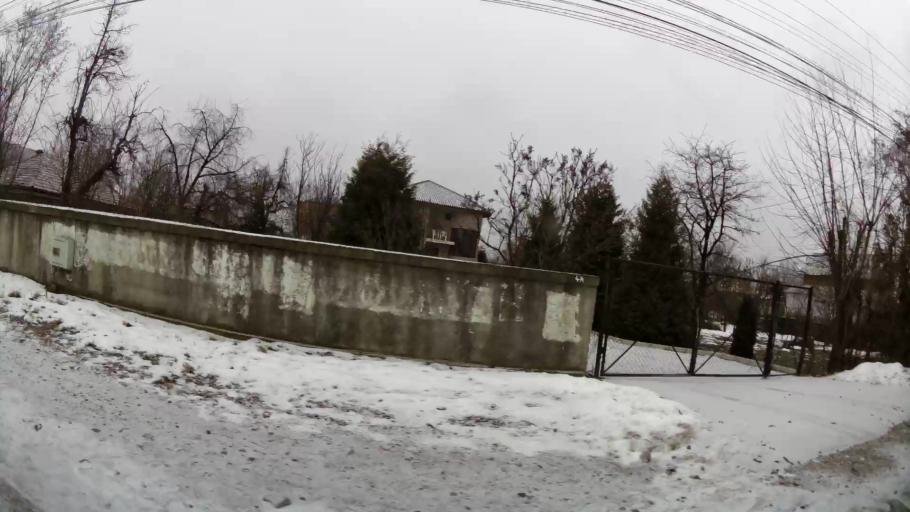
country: RO
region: Dambovita
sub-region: Municipiul Targoviste
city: Targoviste
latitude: 44.9335
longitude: 25.4776
